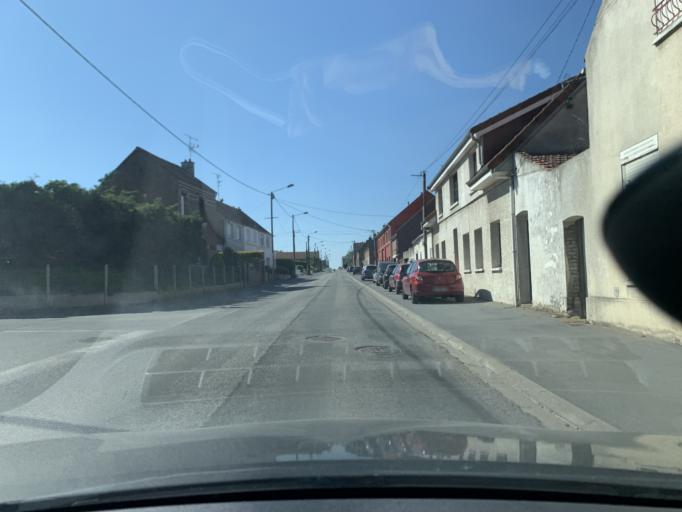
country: FR
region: Nord-Pas-de-Calais
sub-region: Departement du Nord
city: Cambrai
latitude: 50.1579
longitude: 3.2418
